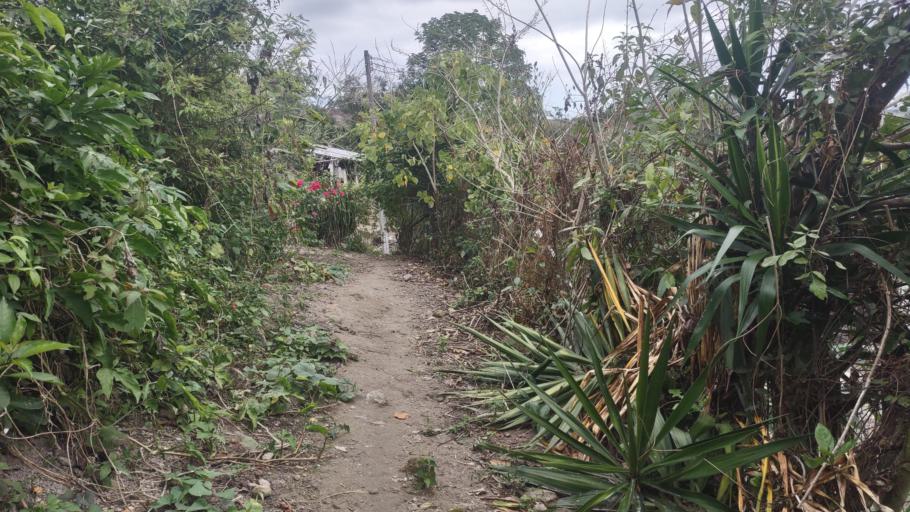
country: MX
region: Veracruz
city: Papantla de Olarte
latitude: 20.4358
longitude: -97.2626
